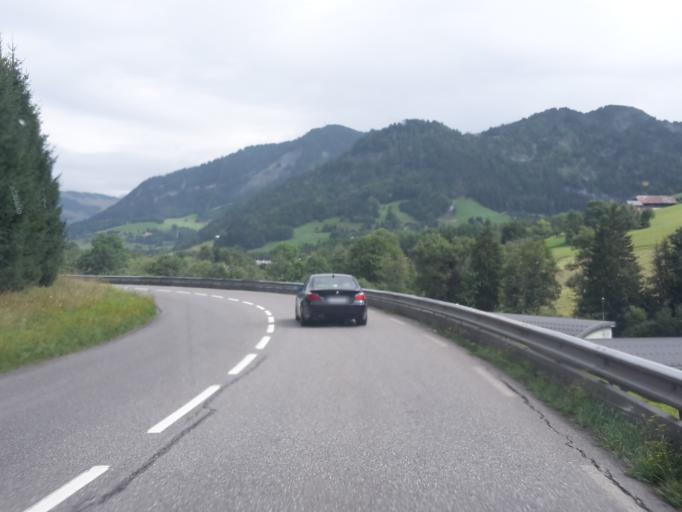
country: FR
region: Rhone-Alpes
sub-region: Departement de la Haute-Savoie
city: Praz-sur-Arly
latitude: 45.8327
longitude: 6.5588
